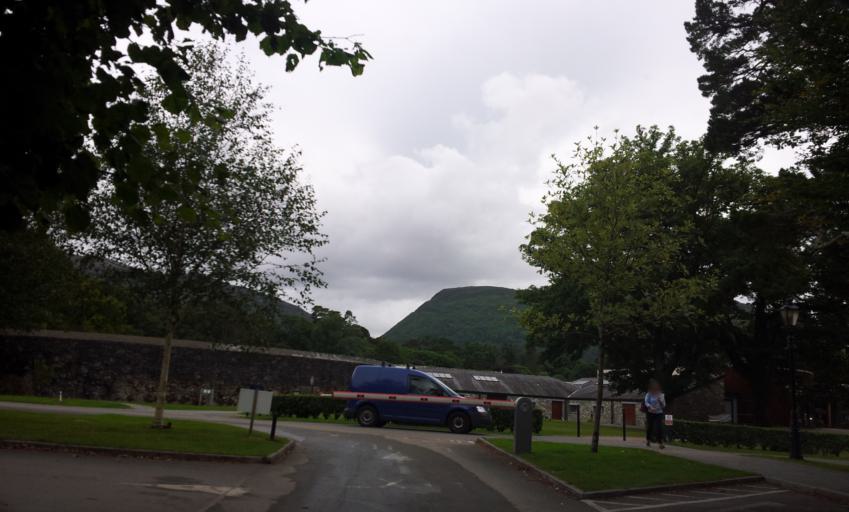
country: IE
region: Munster
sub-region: Ciarrai
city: Cill Airne
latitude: 52.0191
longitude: -9.5010
